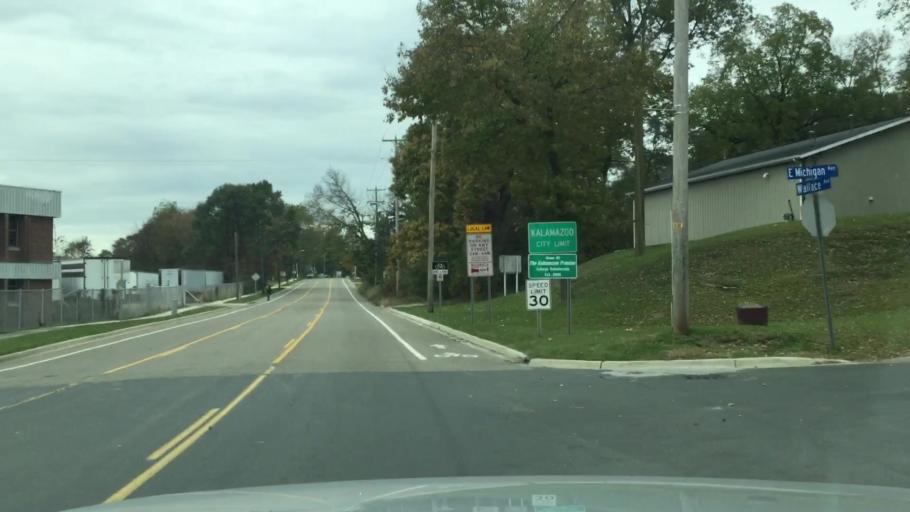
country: US
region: Michigan
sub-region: Kalamazoo County
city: Eastwood
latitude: 42.2920
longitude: -85.5555
